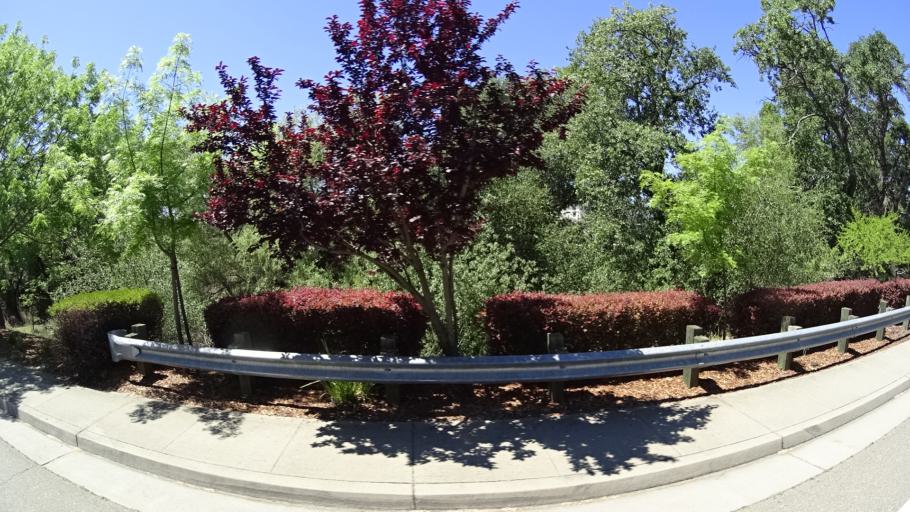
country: US
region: California
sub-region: Placer County
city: Rocklin
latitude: 38.8360
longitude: -121.2470
